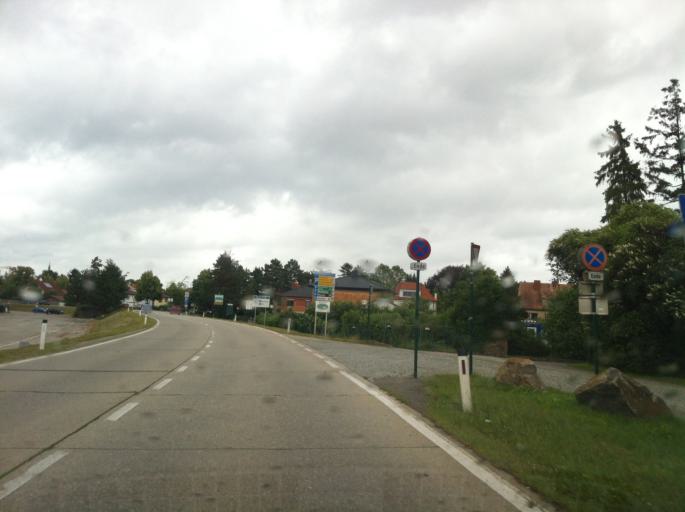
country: AT
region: Lower Austria
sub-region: Politischer Bezirk Tulln
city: Tulln
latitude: 48.3270
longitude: 16.0417
